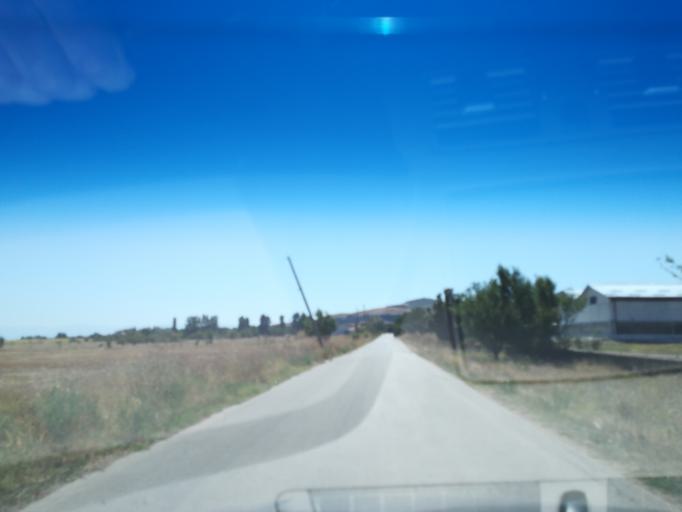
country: BG
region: Pazardzhik
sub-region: Obshtina Pazardzhik
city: Pazardzhik
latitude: 42.3447
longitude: 24.4007
